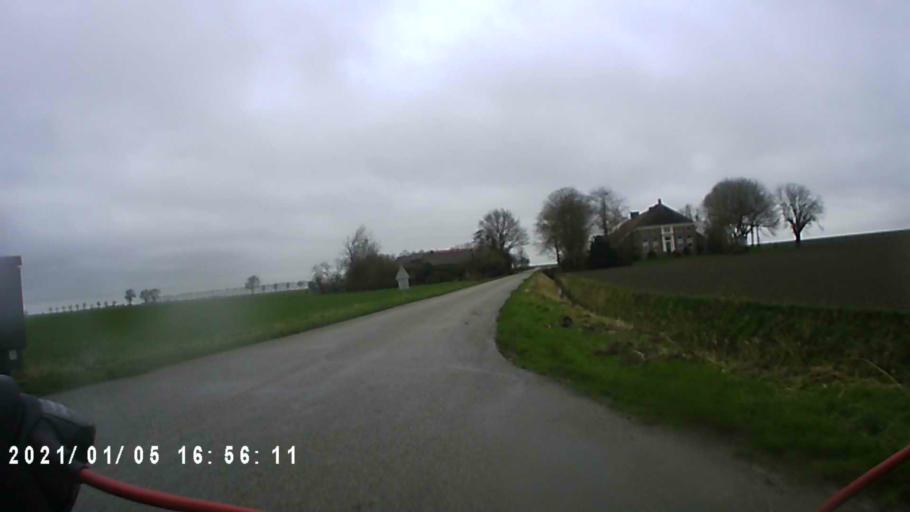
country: NL
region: Groningen
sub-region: Gemeente  Oldambt
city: Winschoten
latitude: 53.2448
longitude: 7.0528
